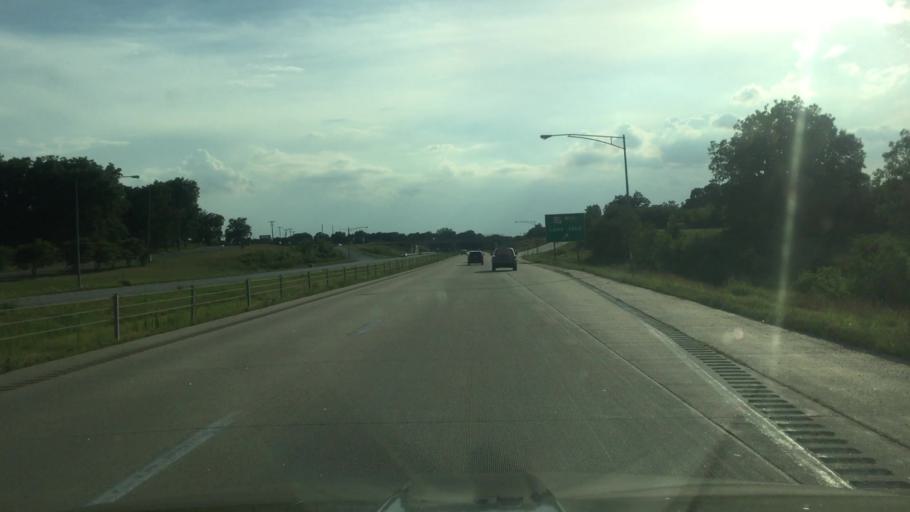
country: US
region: Missouri
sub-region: Jackson County
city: Lone Jack
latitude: 38.8692
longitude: -94.1681
